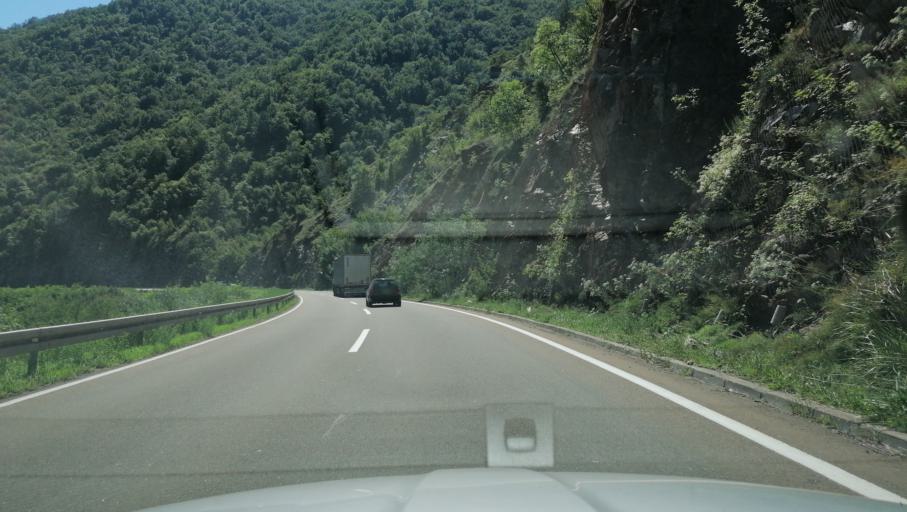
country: RS
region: Central Serbia
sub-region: Raski Okrug
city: Kraljevo
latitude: 43.5524
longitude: 20.6082
